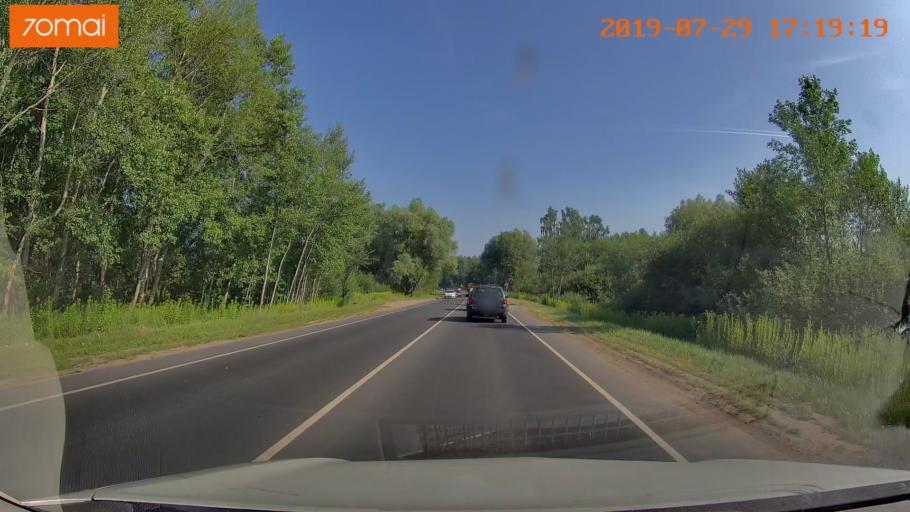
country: RU
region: Kaliningrad
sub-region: Gorod Kaliningrad
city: Kaliningrad
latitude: 54.7720
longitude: 20.4226
